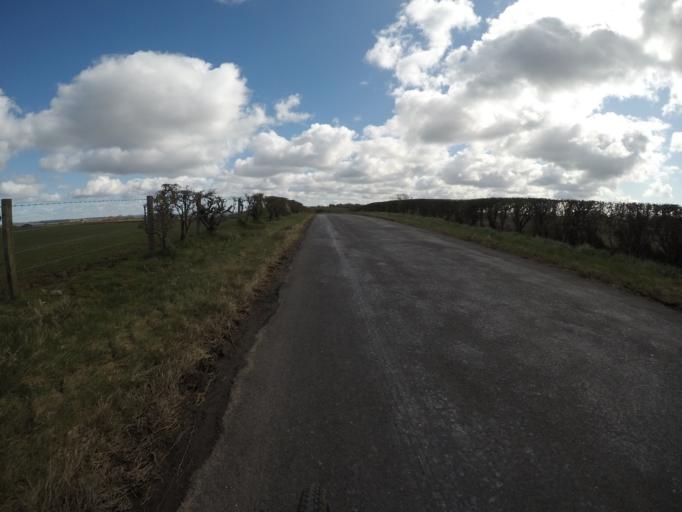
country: GB
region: Scotland
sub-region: South Ayrshire
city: Dundonald
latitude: 55.5899
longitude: -4.5800
